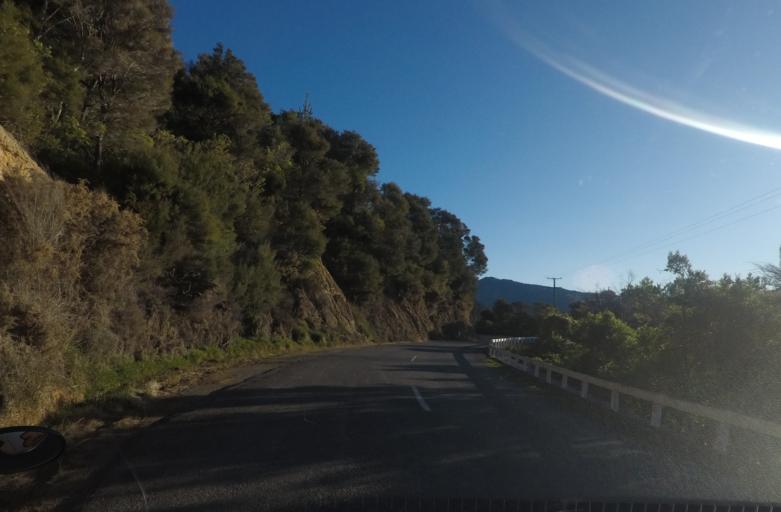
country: NZ
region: Marlborough
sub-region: Marlborough District
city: Picton
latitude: -41.2682
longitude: 173.9567
